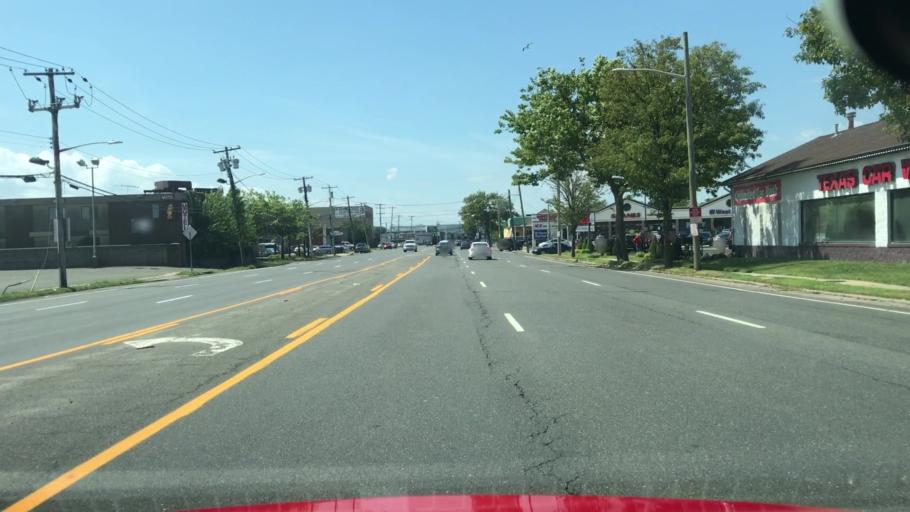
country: US
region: New York
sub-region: Nassau County
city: Barnum Island
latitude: 40.6152
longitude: -73.6432
